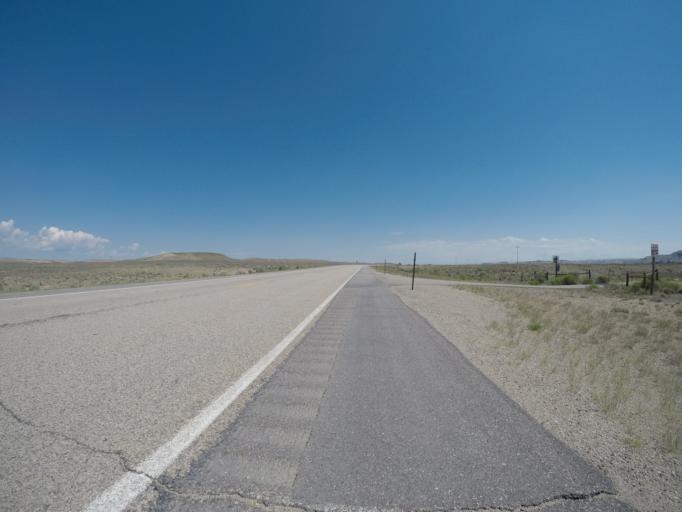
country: US
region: Wyoming
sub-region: Sublette County
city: Marbleton
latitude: 42.4250
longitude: -110.1105
